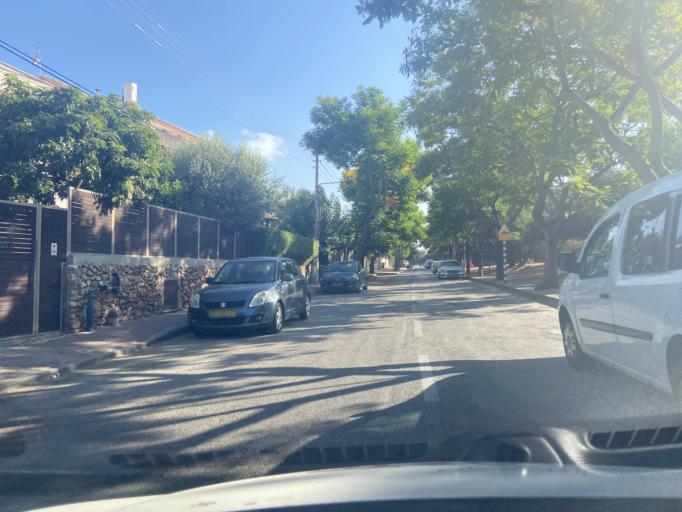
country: IL
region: Central District
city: Yehud
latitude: 32.0380
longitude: 34.8940
